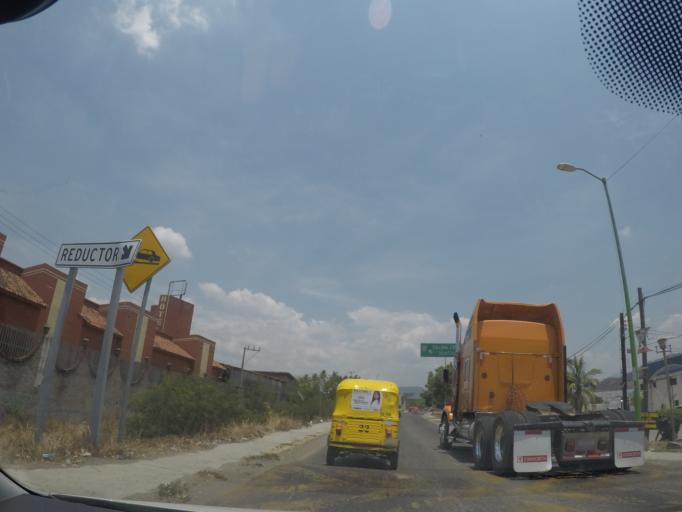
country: MX
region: Oaxaca
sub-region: Santo Domingo Tehuantepec
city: Santo Domingo Tehuantepec
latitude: 16.3242
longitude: -95.2409
